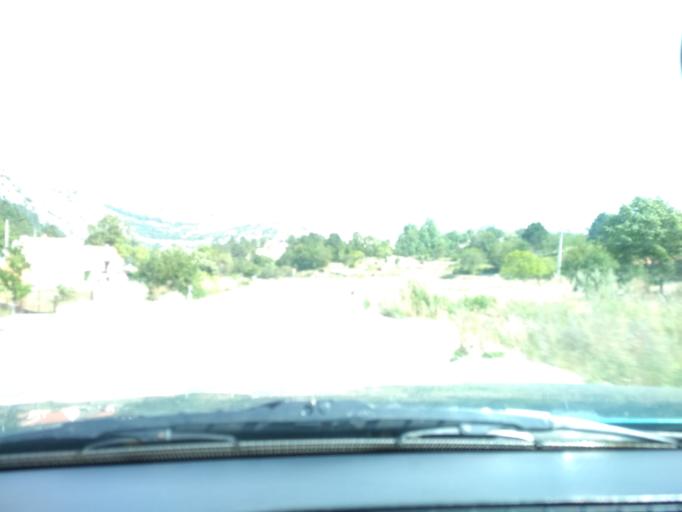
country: ME
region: Kotor
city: Kotor
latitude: 42.4296
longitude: 18.8057
